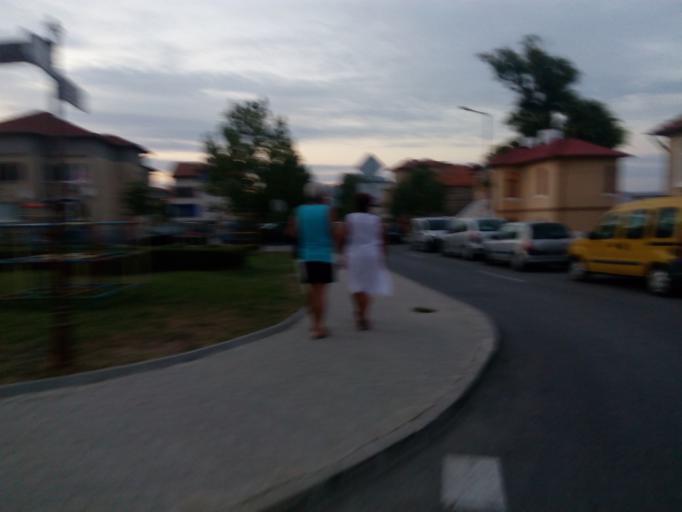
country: BG
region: Burgas
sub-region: Obshtina Nesebur
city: Obzor
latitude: 42.8166
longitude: 27.8848
